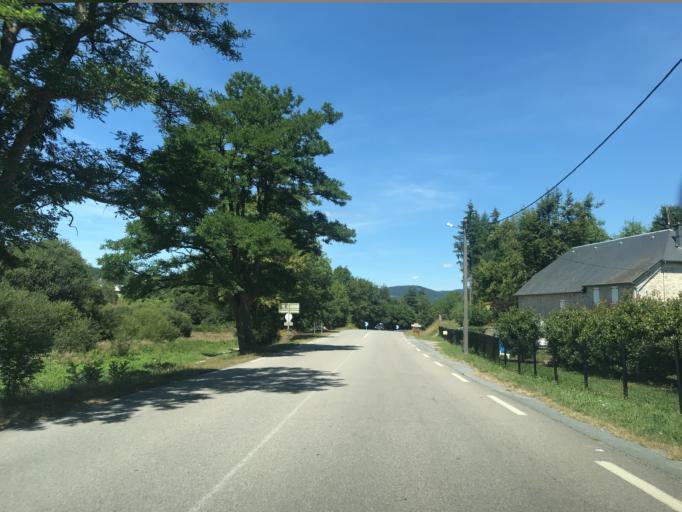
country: FR
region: Limousin
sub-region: Departement de la Correze
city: Egletons
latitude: 45.4084
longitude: 2.0515
